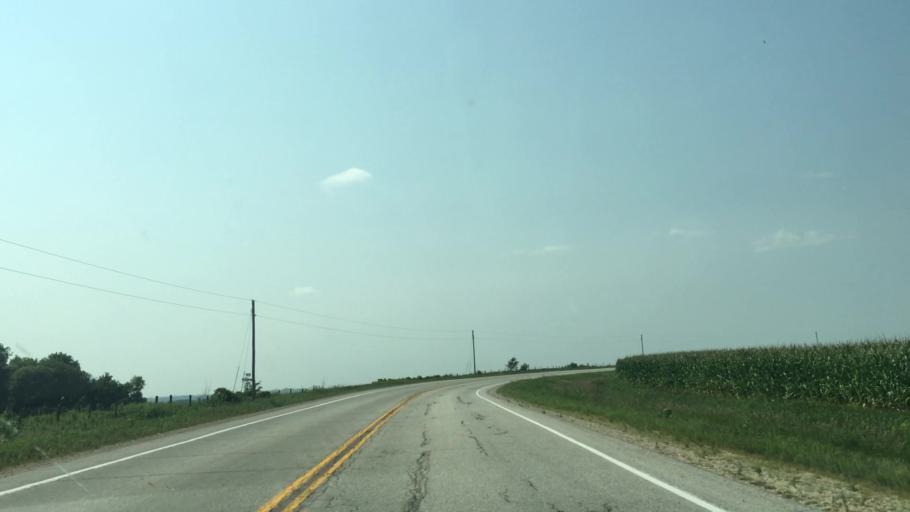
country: US
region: Minnesota
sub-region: Fillmore County
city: Harmony
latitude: 43.6670
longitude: -91.9350
